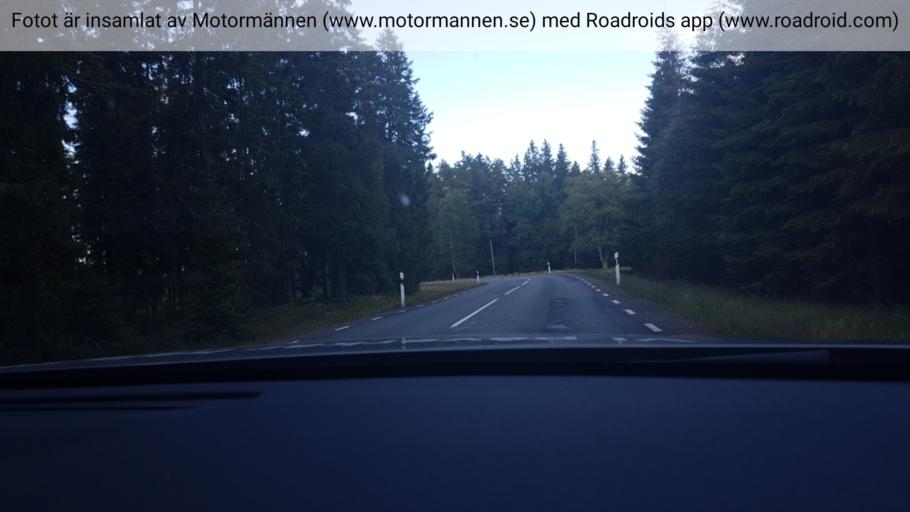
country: SE
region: Joenkoeping
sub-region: Gnosjo Kommun
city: Gnosjoe
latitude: 57.5886
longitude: 13.6887
